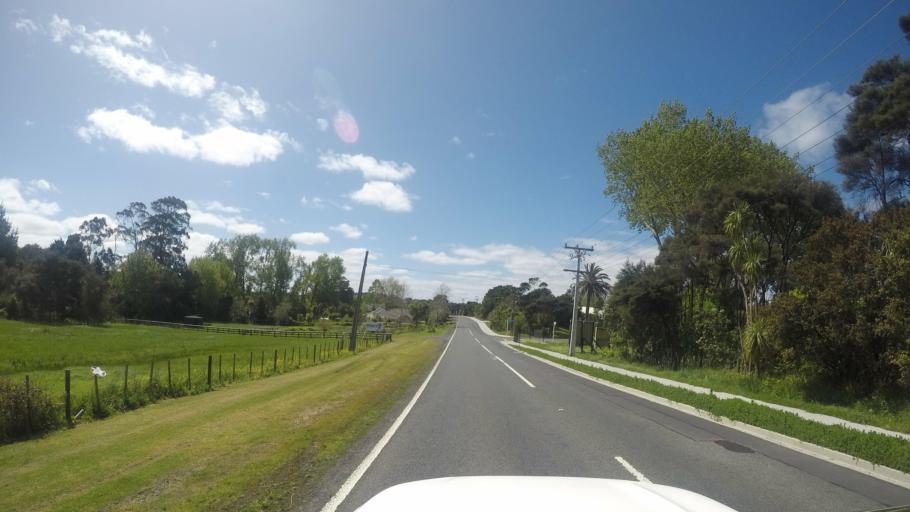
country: NZ
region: Auckland
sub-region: Auckland
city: Muriwai Beach
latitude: -36.7748
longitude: 174.4889
